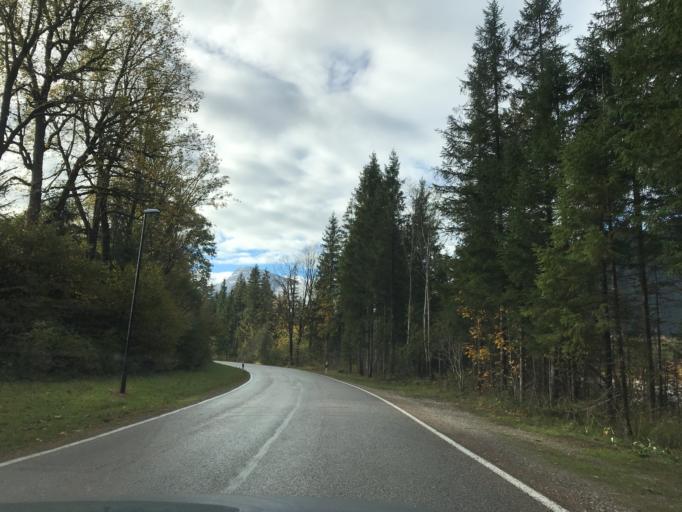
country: DE
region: Bavaria
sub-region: Upper Bavaria
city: Jachenau
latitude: 47.5580
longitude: 11.4346
